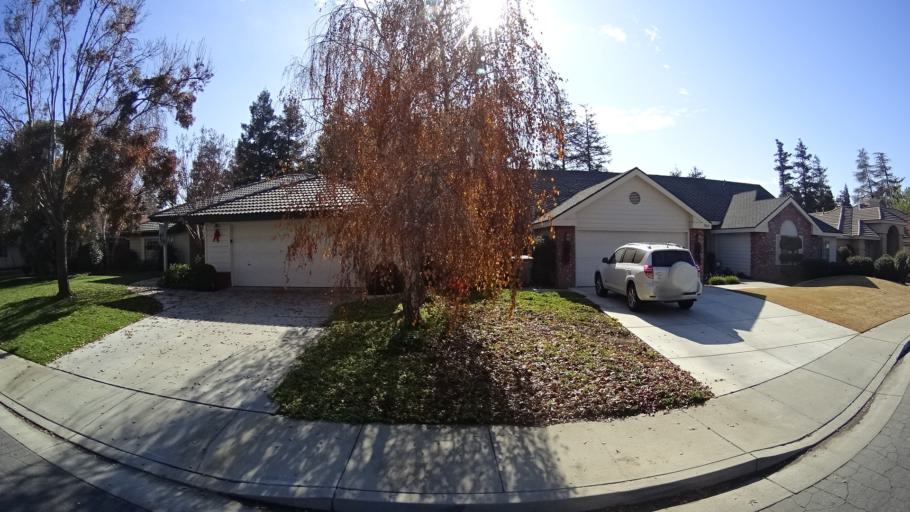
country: US
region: California
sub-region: Kern County
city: Greenacres
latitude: 35.4021
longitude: -119.0901
